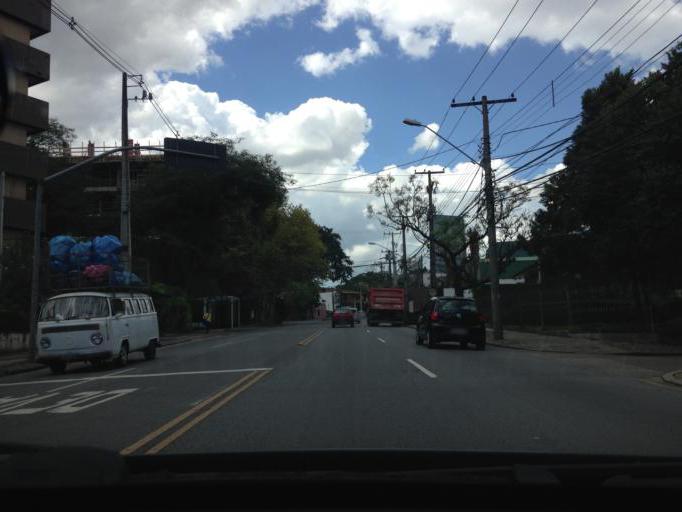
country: BR
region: Parana
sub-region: Curitiba
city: Curitiba
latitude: -25.4064
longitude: -49.2479
